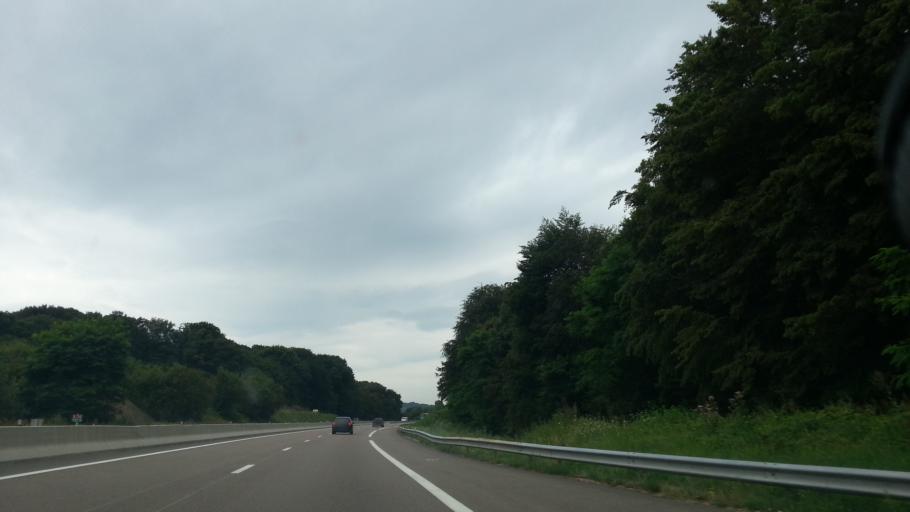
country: FR
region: Franche-Comte
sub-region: Departement du Doubs
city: Dannemarie-sur-Crete
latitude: 47.2148
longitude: 5.8553
